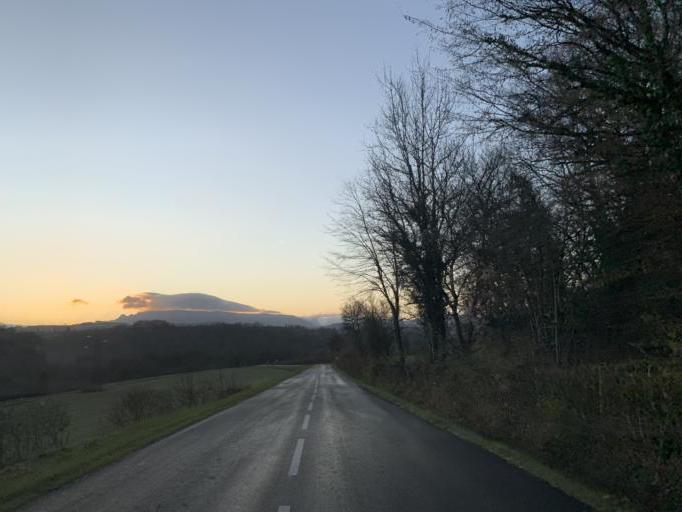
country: FR
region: Rhone-Alpes
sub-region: Departement de l'Ain
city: Belley
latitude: 45.7819
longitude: 5.6562
